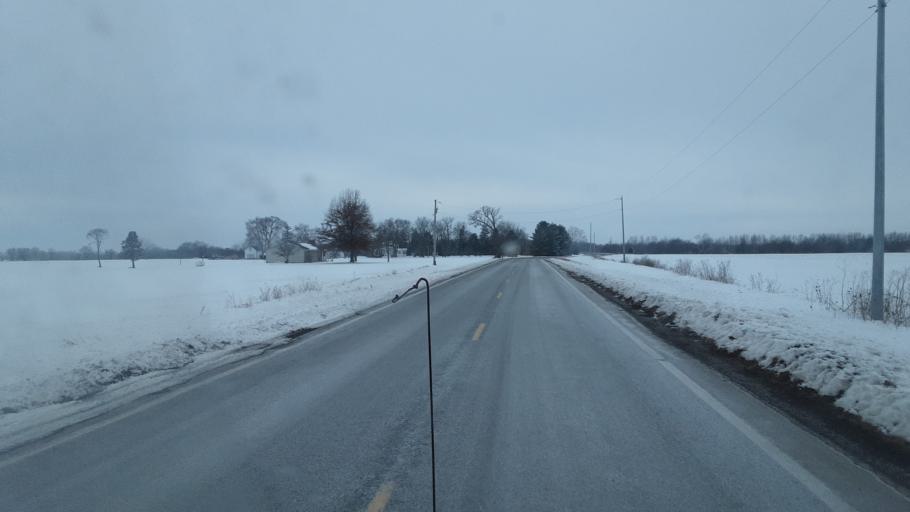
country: US
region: Ohio
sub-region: Champaign County
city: Mechanicsburg
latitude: 40.1208
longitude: -83.4475
